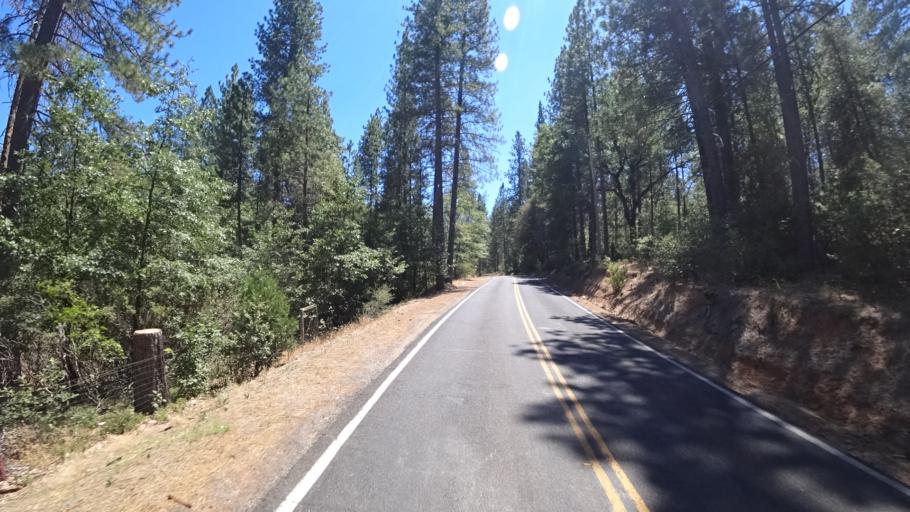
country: US
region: California
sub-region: Calaveras County
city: Mountain Ranch
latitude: 38.3148
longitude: -120.5205
